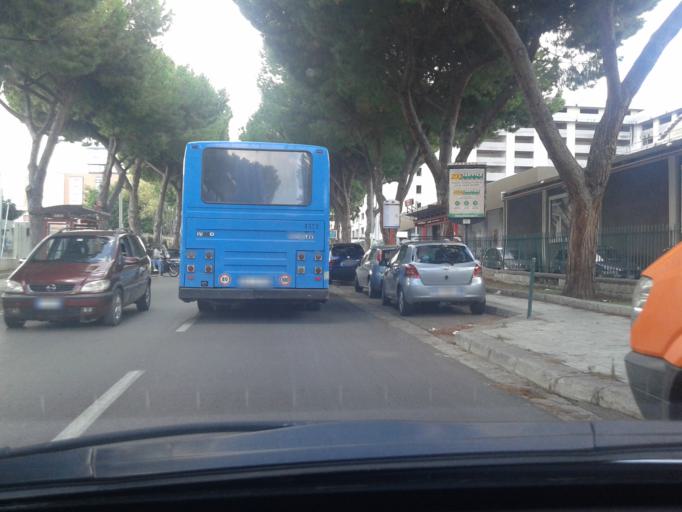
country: IT
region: Sicily
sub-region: Palermo
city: Palermo
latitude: 38.1570
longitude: 13.3183
